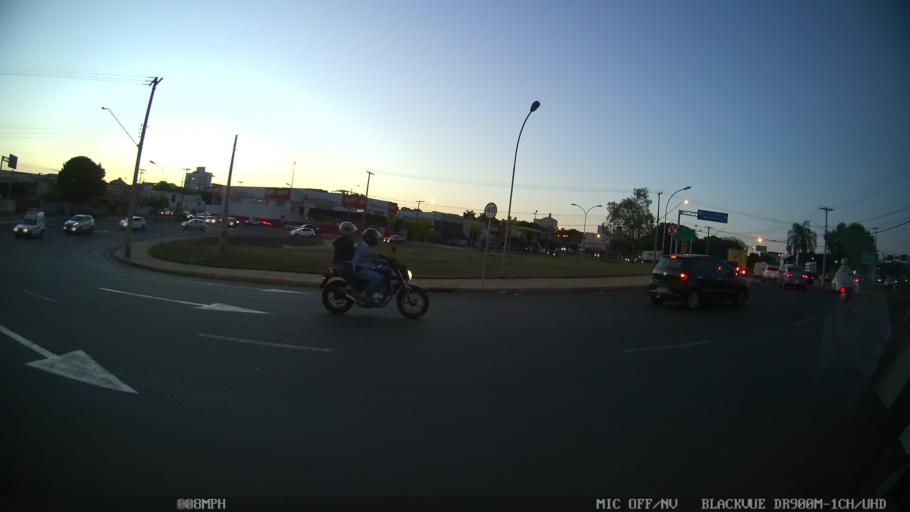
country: BR
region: Sao Paulo
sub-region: Sao Jose Do Rio Preto
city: Sao Jose do Rio Preto
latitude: -20.8036
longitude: -49.3596
